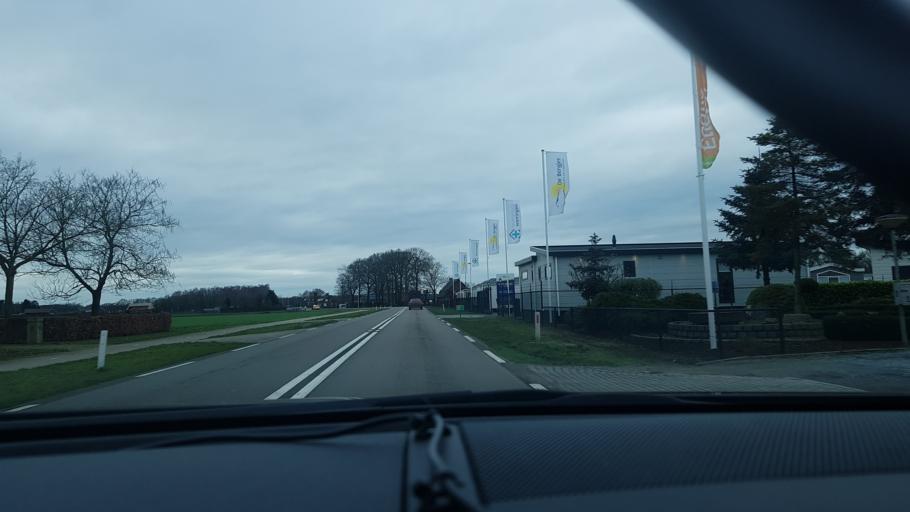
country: NL
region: Limburg
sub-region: Gemeente Leudal
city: Heythuysen
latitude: 51.2860
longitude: 5.9080
